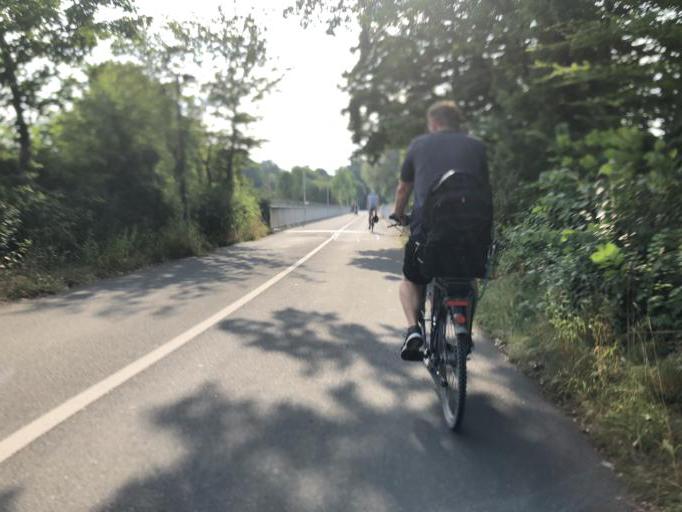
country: DE
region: Bavaria
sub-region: Regierungsbezirk Mittelfranken
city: Erlangen
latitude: 49.5873
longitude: 10.9785
